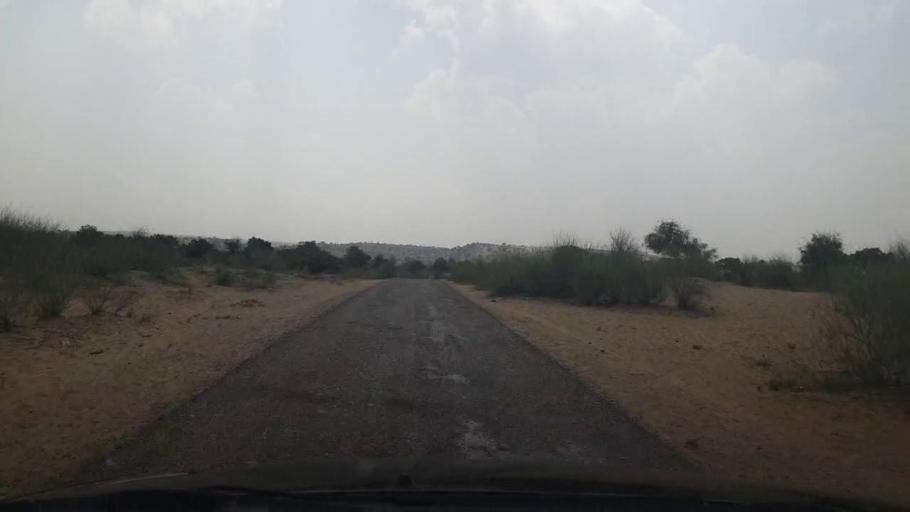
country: PK
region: Sindh
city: Islamkot
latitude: 24.9965
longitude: 70.4979
